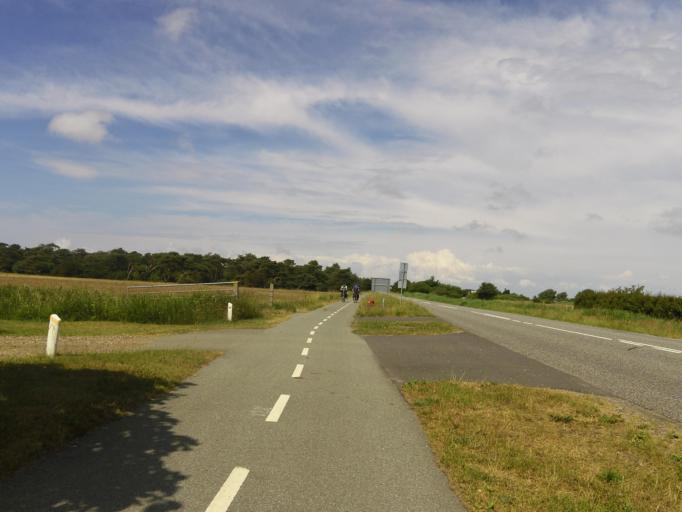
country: DE
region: Schleswig-Holstein
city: List
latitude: 55.1531
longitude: 8.5496
